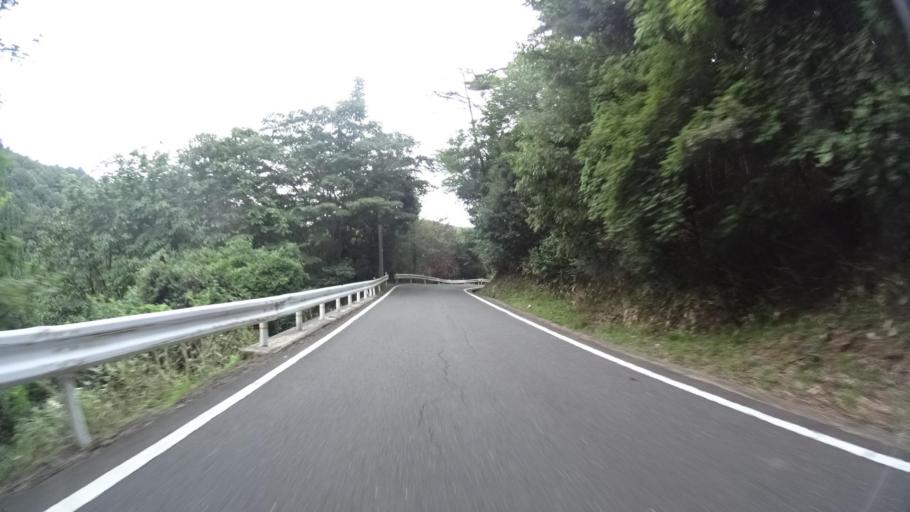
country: JP
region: Kyoto
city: Miyazu
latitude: 35.4709
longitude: 135.1502
